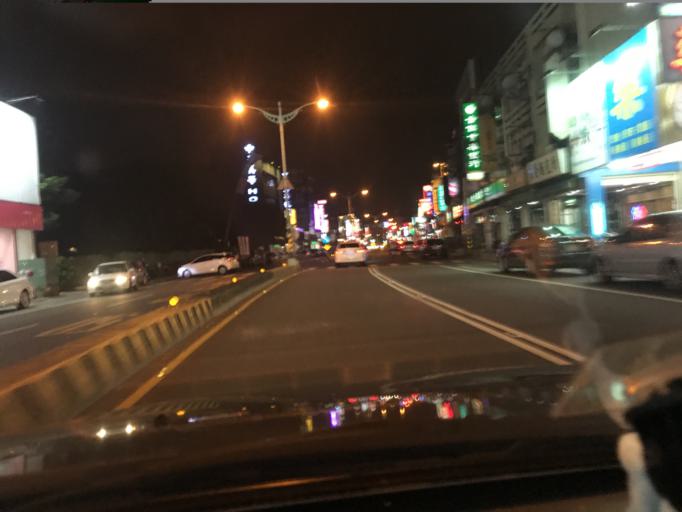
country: TW
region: Taiwan
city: Daxi
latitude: 24.8635
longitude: 121.2172
